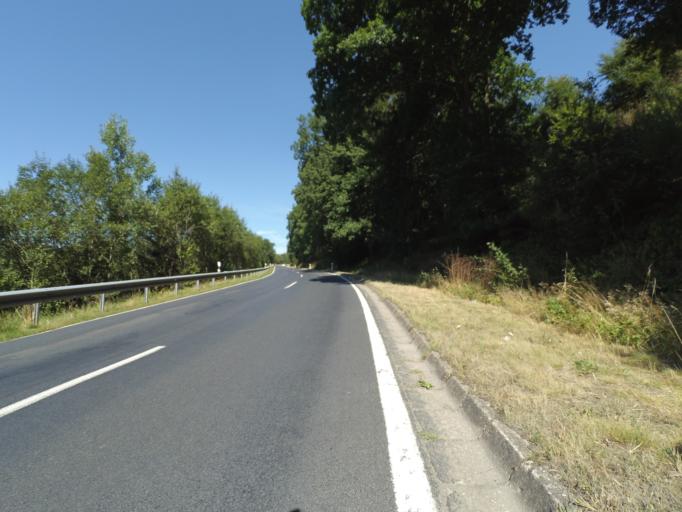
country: DE
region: Rheinland-Pfalz
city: Mullenbach
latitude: 50.2101
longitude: 7.0592
